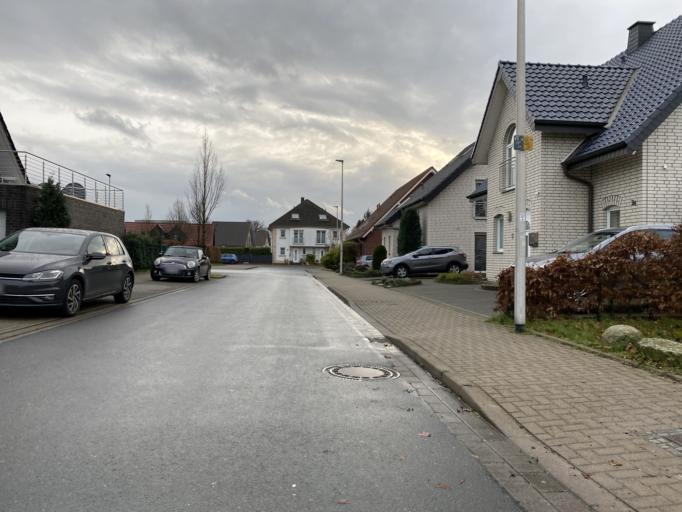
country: DE
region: North Rhine-Westphalia
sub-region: Regierungsbezirk Arnsberg
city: Hamm
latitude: 51.6834
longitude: 7.8660
